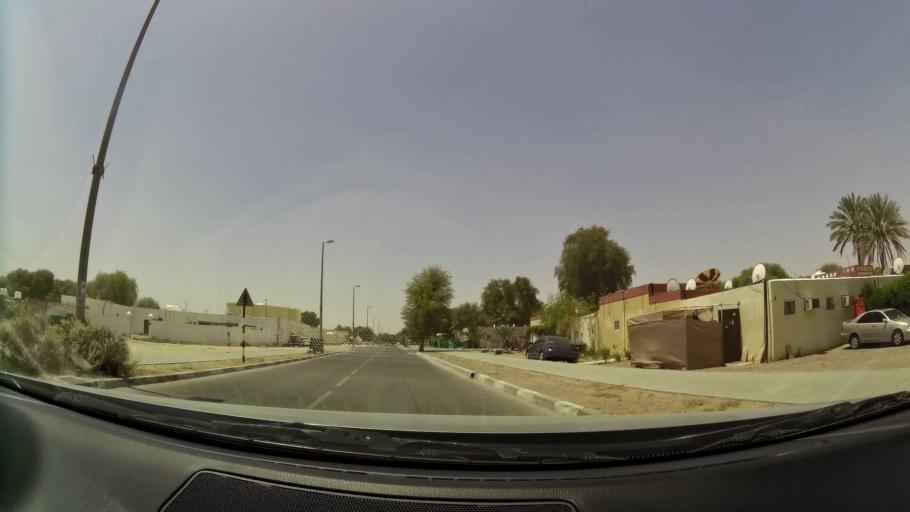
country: OM
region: Al Buraimi
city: Al Buraymi
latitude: 24.2744
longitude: 55.7455
